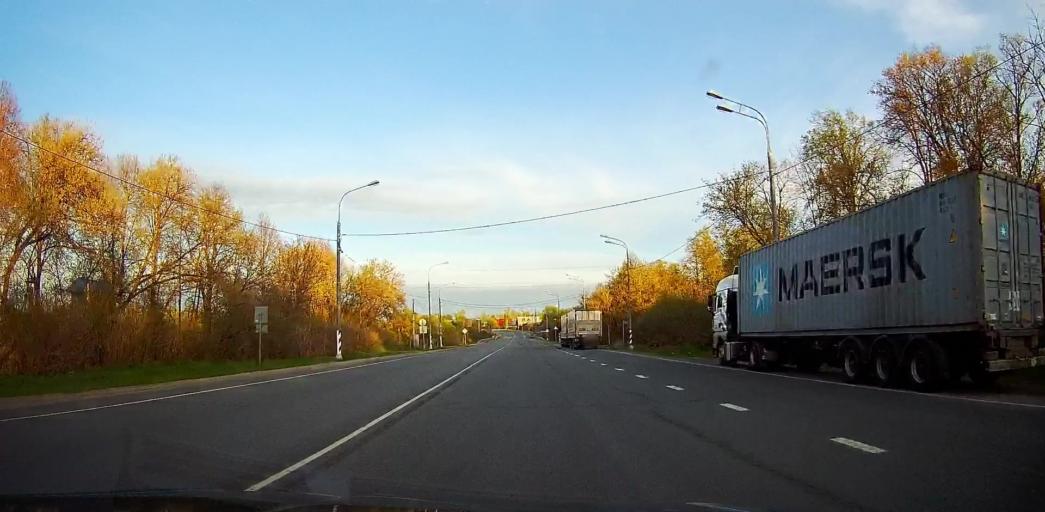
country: RU
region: Moskovskaya
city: Troitskoye
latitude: 55.2282
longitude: 38.5570
